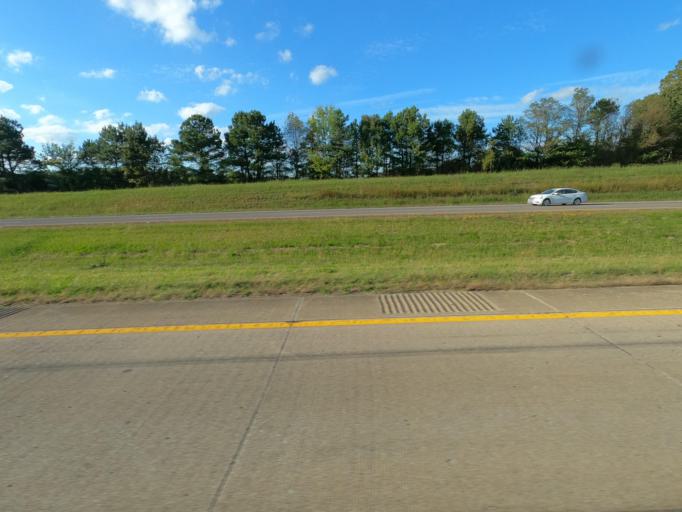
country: US
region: Tennessee
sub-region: Gibson County
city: Medina
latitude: 35.6947
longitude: -88.7008
